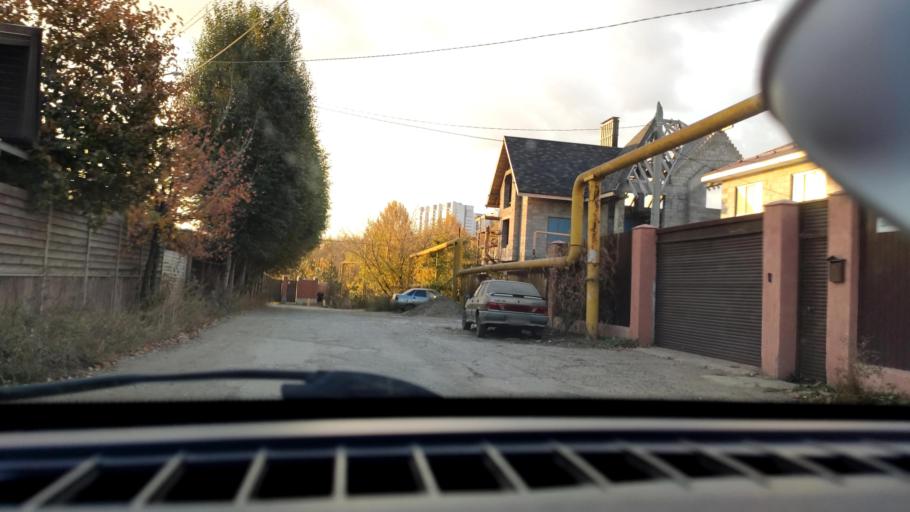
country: RU
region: Samara
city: Samara
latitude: 53.2721
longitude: 50.2292
